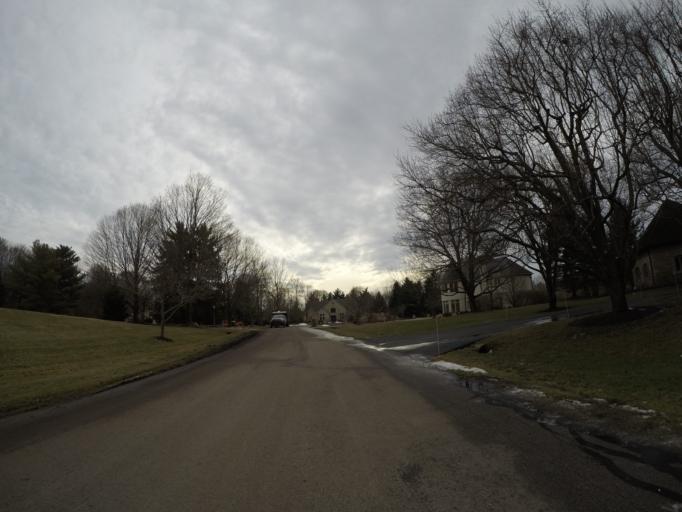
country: US
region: Ohio
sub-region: Franklin County
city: Dublin
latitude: 40.0560
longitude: -83.0927
